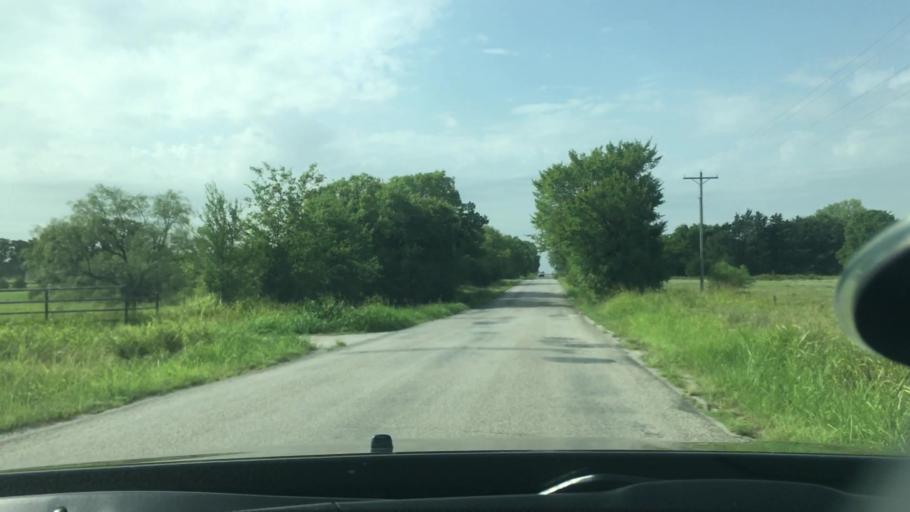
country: US
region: Oklahoma
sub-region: Carter County
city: Lone Grove
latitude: 34.2072
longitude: -97.2650
